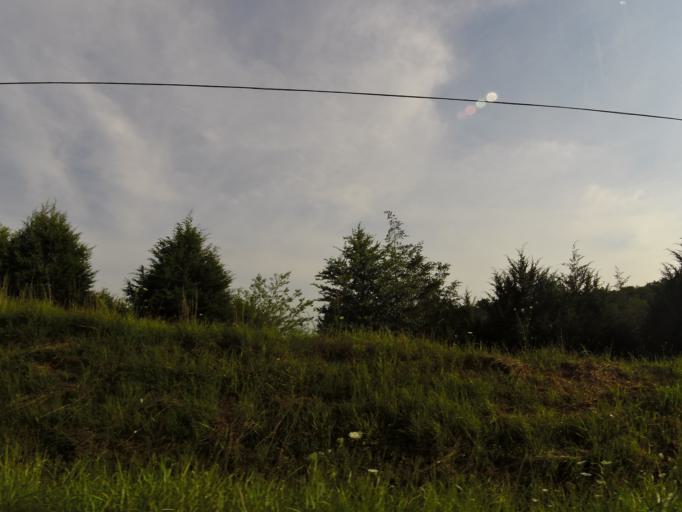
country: US
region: Tennessee
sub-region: Humphreys County
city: McEwen
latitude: 36.0981
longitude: -87.6014
